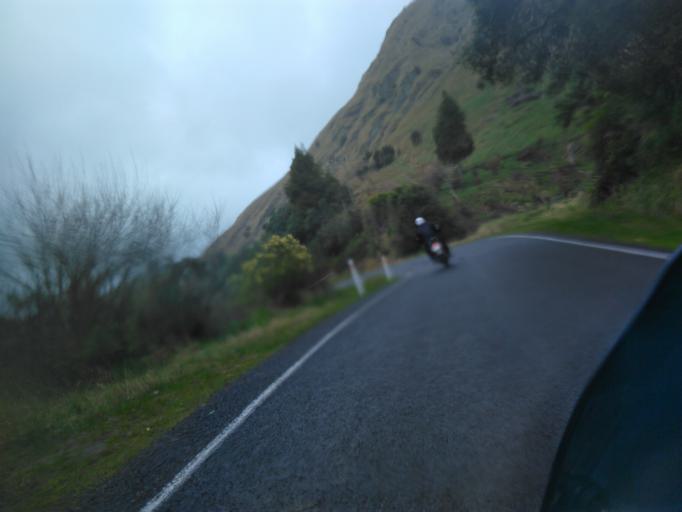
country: NZ
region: Gisborne
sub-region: Gisborne District
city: Gisborne
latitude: -38.6717
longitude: 177.7179
